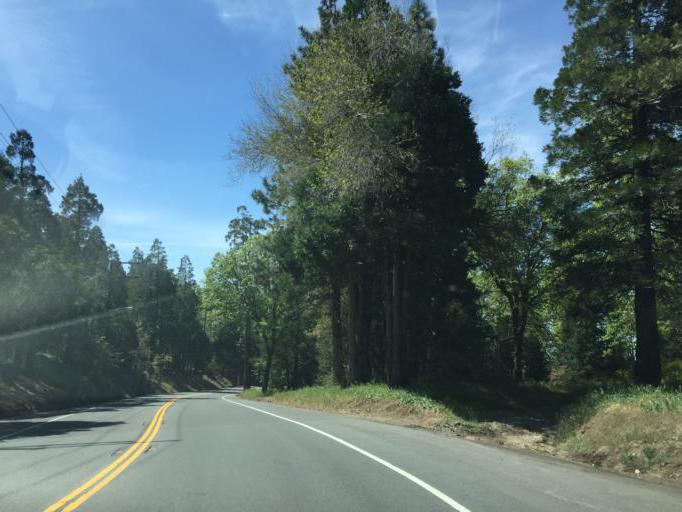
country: US
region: California
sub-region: San Bernardino County
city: Crestline
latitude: 34.2364
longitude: -117.2426
